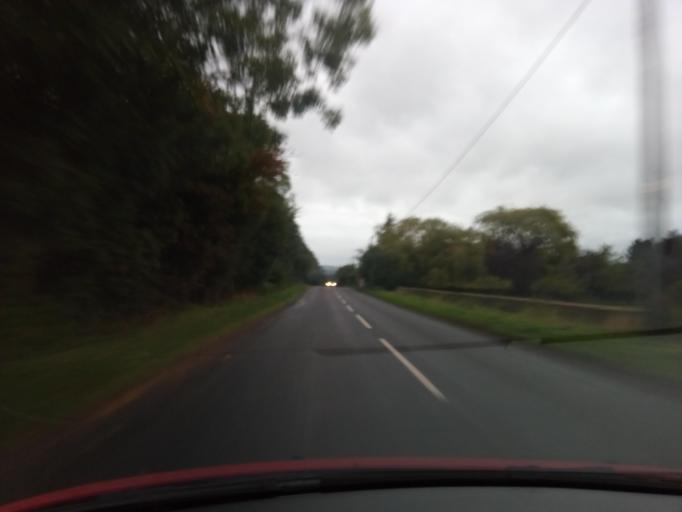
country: GB
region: England
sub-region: Darlington
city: High Coniscliffe
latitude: 54.5254
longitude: -1.6720
